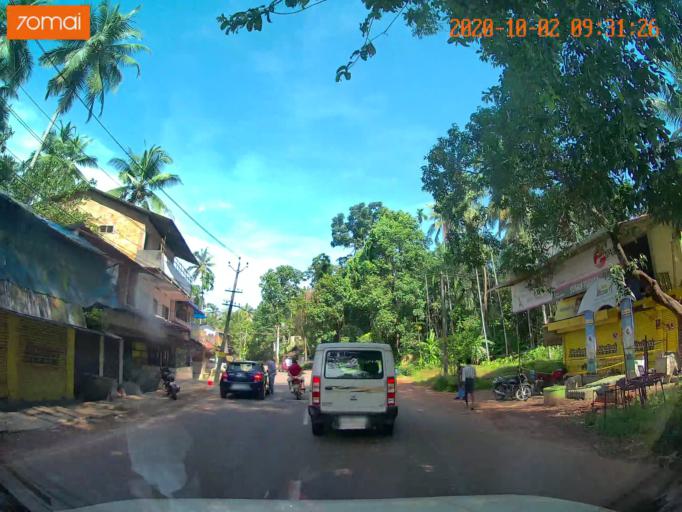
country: IN
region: Kerala
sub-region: Kozhikode
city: Nadapuram
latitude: 11.6240
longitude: 75.7605
